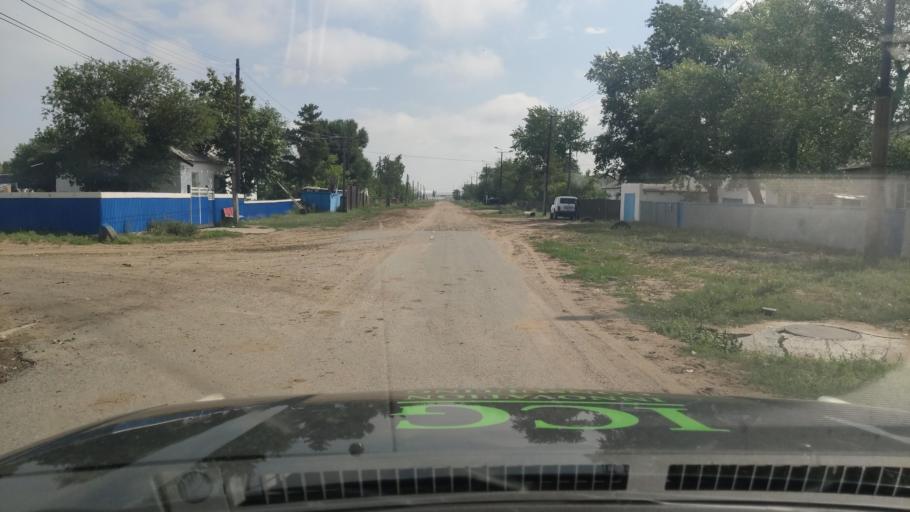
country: KZ
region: Pavlodar
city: Koktobe
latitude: 51.9660
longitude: 77.6427
